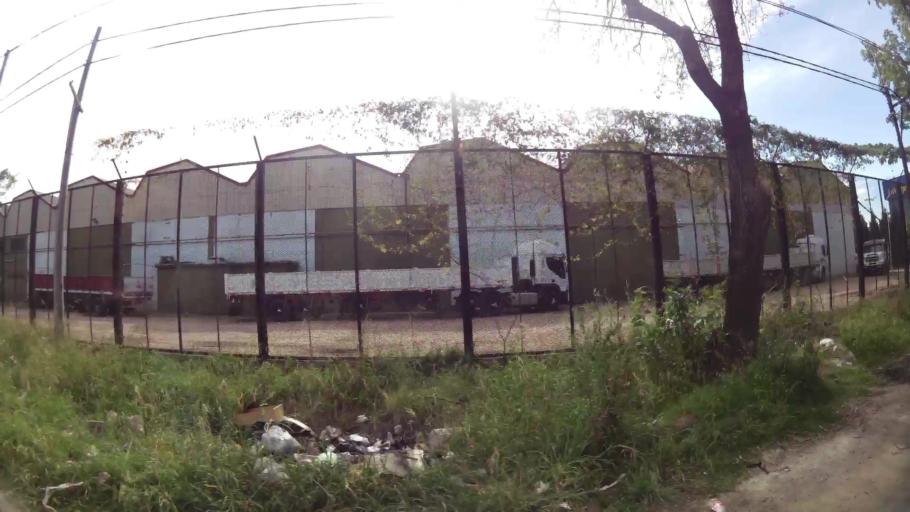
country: AR
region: Santa Fe
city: Granadero Baigorria
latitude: -32.9144
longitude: -60.7214
